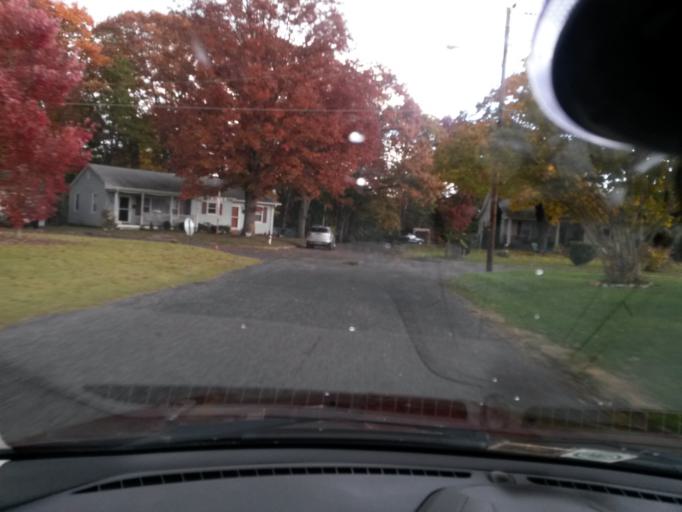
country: US
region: Virginia
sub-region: Alleghany County
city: Clifton Forge
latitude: 37.8245
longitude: -79.8185
